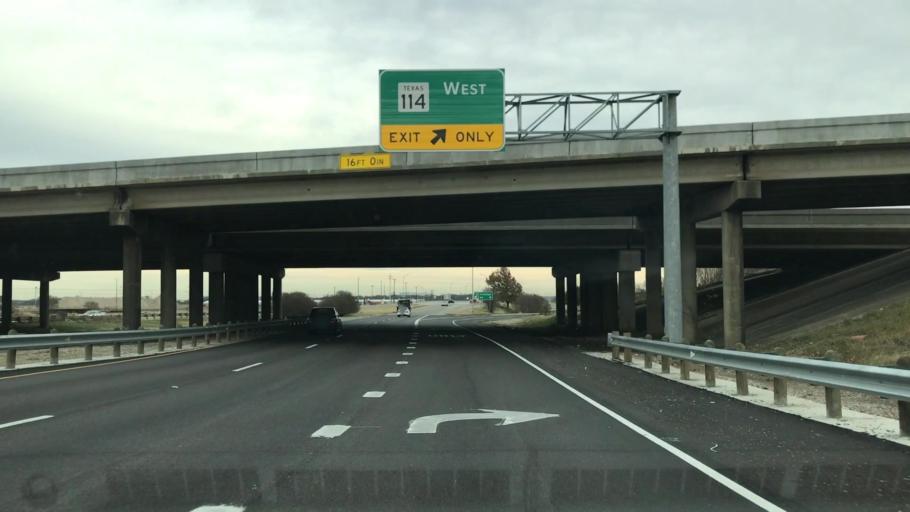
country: US
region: Texas
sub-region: Dallas County
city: Irving
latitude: 32.8382
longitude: -96.9054
